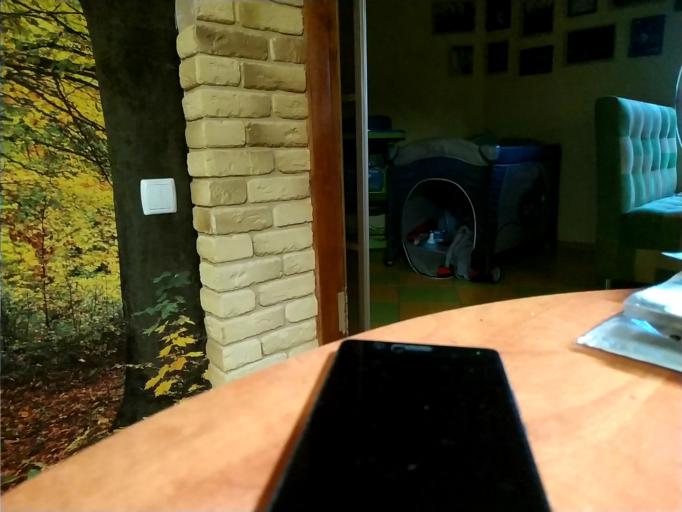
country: RU
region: Orjol
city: Znamenskoye
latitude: 53.4303
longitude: 35.5338
